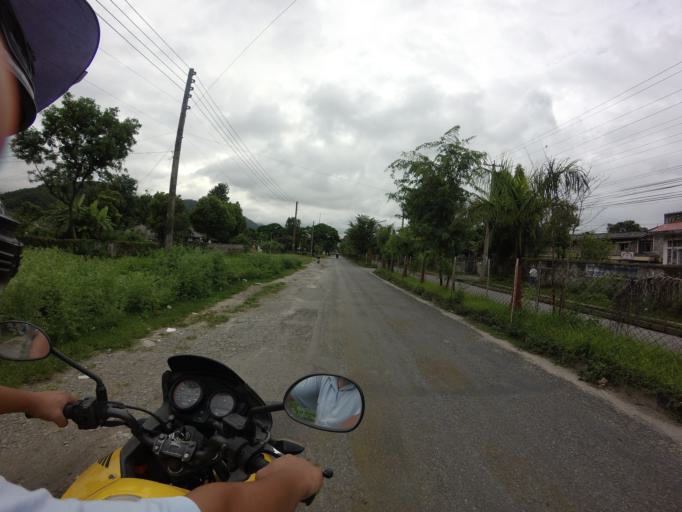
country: NP
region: Western Region
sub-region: Gandaki Zone
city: Pokhara
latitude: 28.1996
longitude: 83.9735
